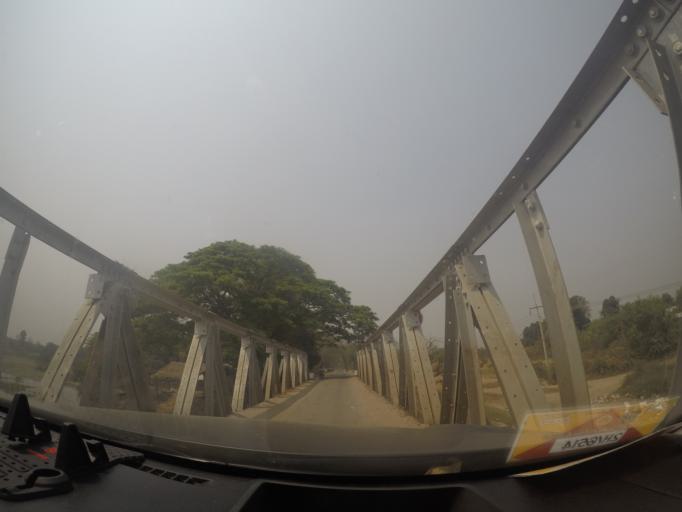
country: MM
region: Magway
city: Taungdwingyi
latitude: 19.8688
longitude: 95.5158
